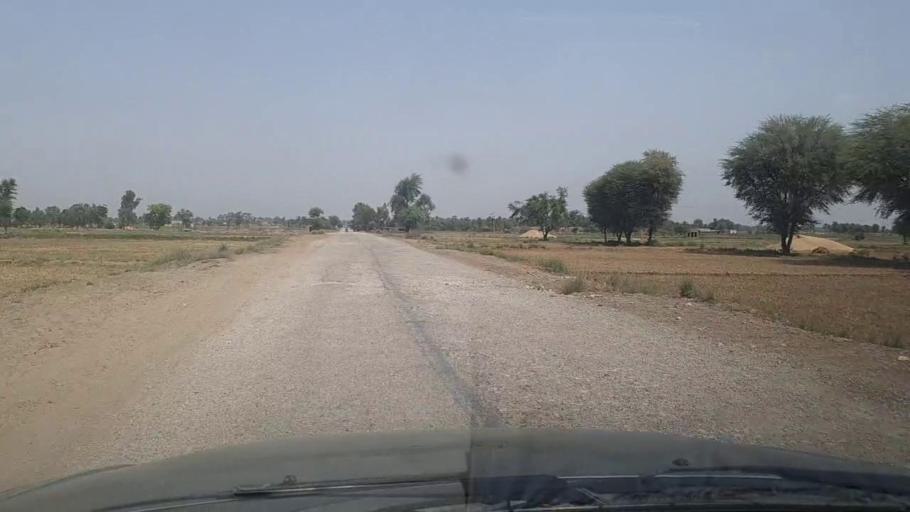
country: PK
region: Sindh
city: Setharja Old
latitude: 27.1576
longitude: 68.5202
